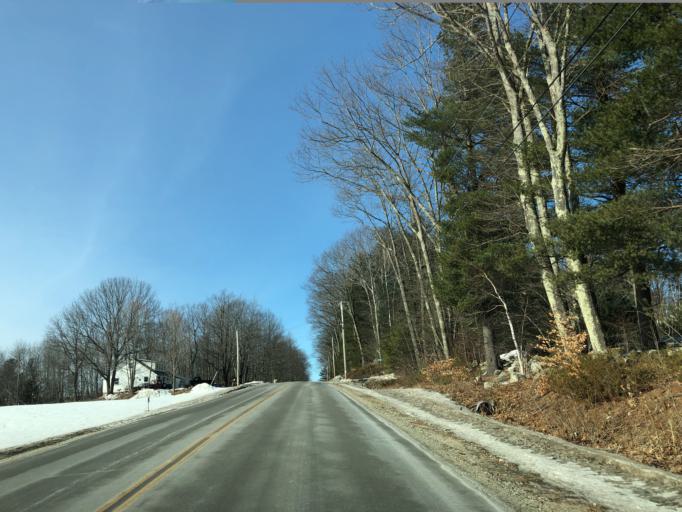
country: US
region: Maine
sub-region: Androscoggin County
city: Mechanic Falls
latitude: 44.1528
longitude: -70.3400
